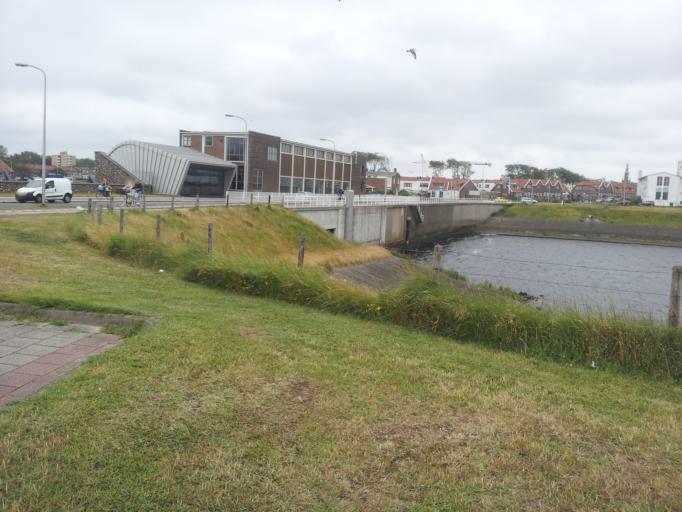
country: NL
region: South Holland
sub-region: Gemeente Katwijk
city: Katwijk aan Zee
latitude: 52.2086
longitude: 4.4065
